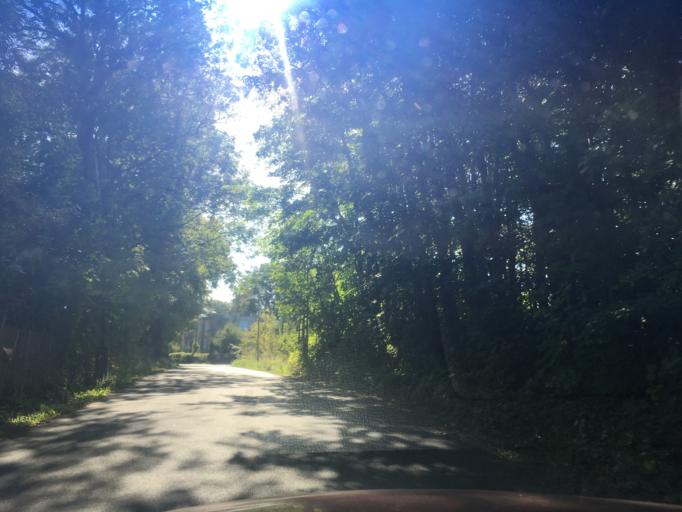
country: PL
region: Lower Silesian Voivodeship
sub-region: Powiat lubanski
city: Siekierczyn
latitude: 51.0376
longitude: 15.1730
